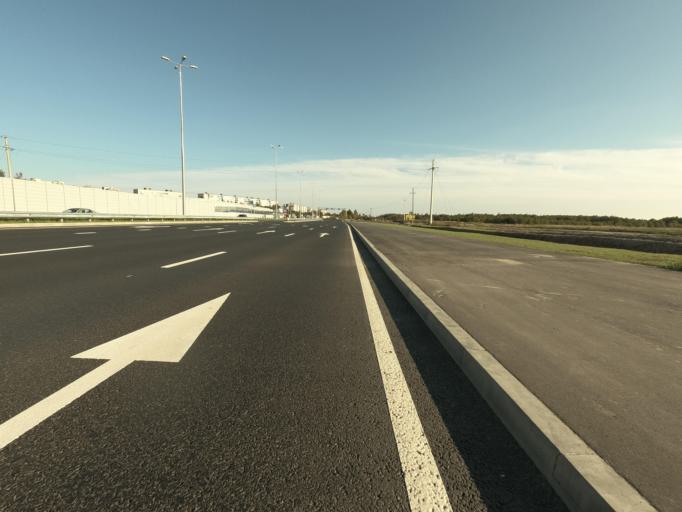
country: RU
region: St.-Petersburg
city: Kolpino
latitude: 59.7378
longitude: 30.5539
